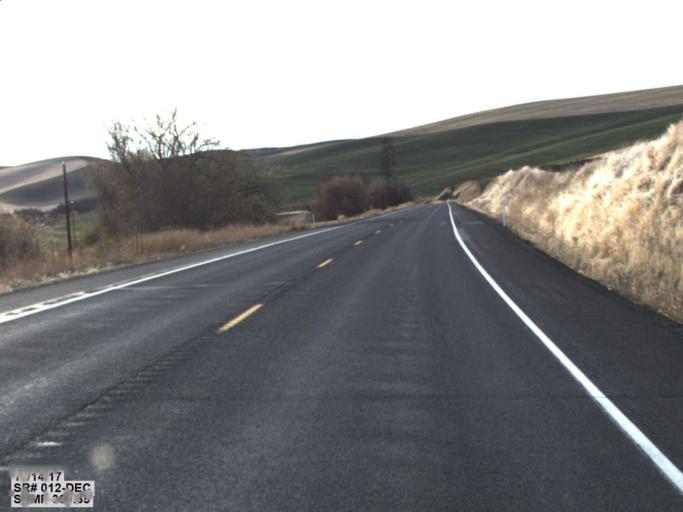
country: US
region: Washington
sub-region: Columbia County
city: Dayton
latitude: 46.3490
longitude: -117.9718
